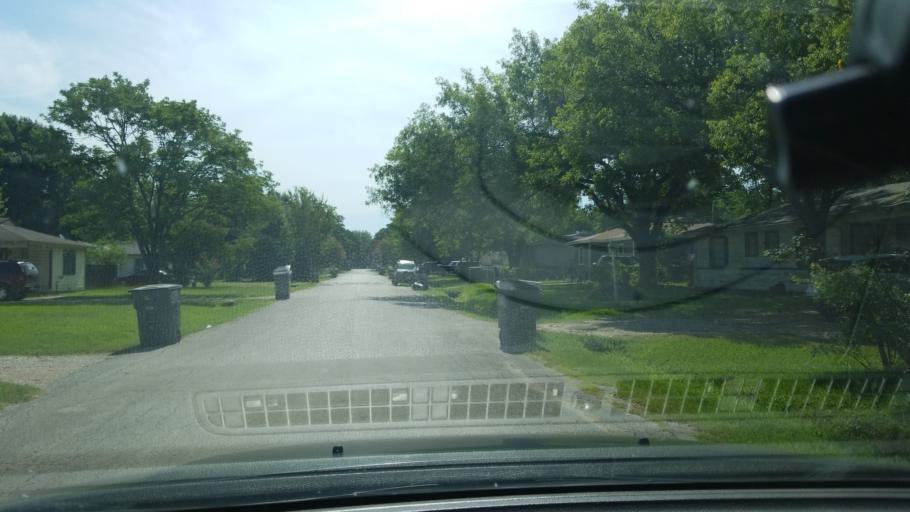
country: US
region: Texas
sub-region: Dallas County
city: Balch Springs
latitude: 32.7309
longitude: -96.6251
